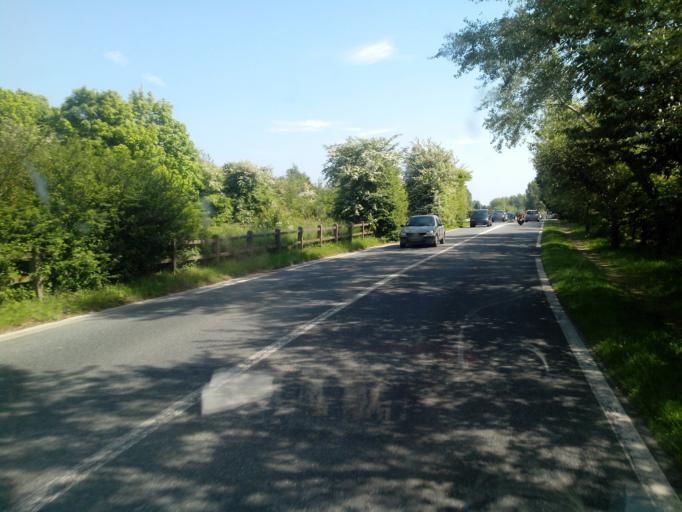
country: FR
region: Nord-Pas-de-Calais
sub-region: Departement du Pas-de-Calais
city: Verton
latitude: 50.3753
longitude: 1.6592
